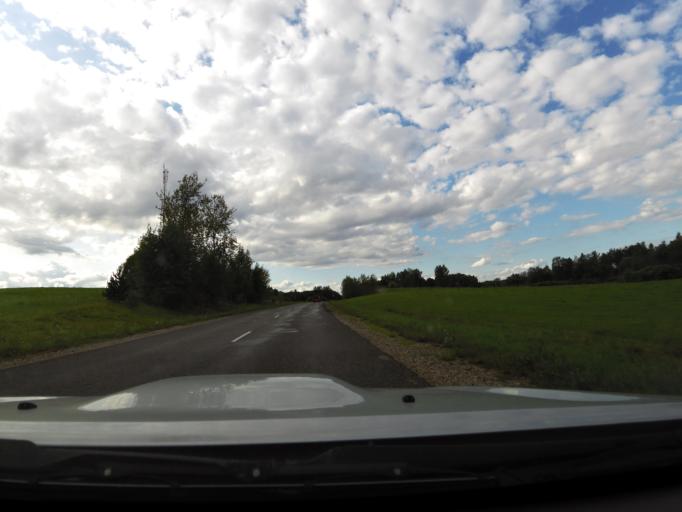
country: LV
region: Akniste
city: Akniste
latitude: 56.0134
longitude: 25.9285
